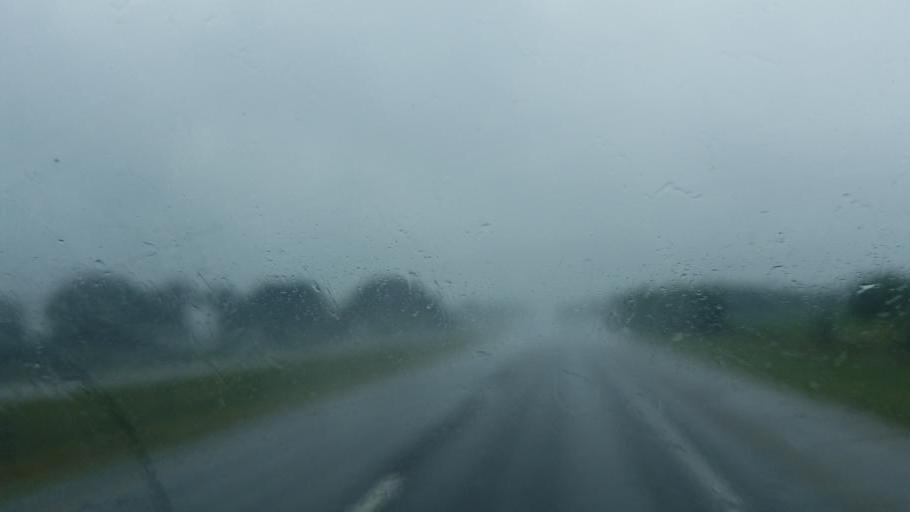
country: US
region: Indiana
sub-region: Delaware County
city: Yorktown
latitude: 40.2651
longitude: -85.5579
